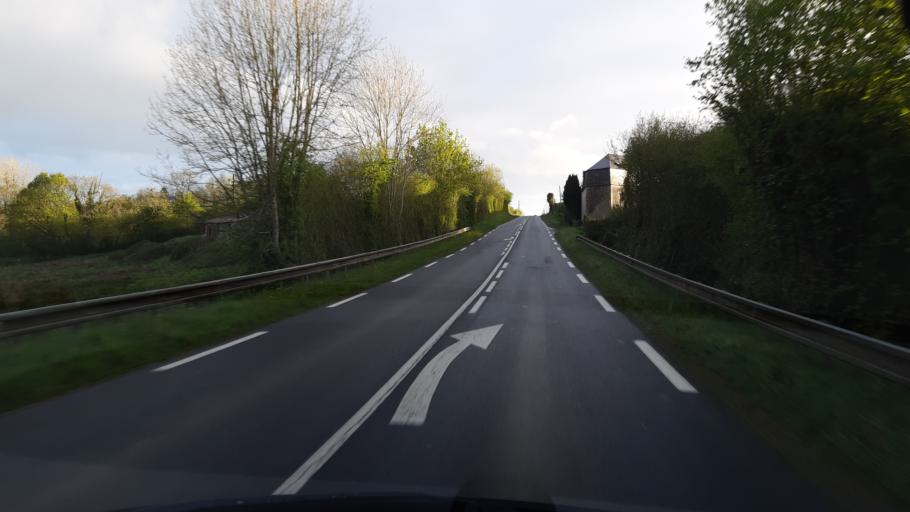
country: FR
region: Lower Normandy
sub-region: Departement de la Manche
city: Percy
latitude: 49.0041
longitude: -1.1524
